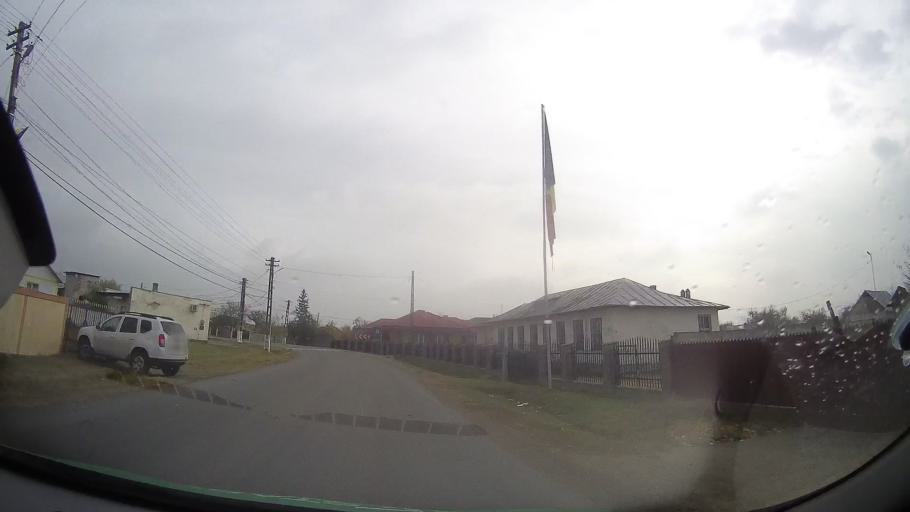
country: RO
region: Prahova
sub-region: Comuna Rafov
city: Palanca
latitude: 44.8416
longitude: 26.2380
